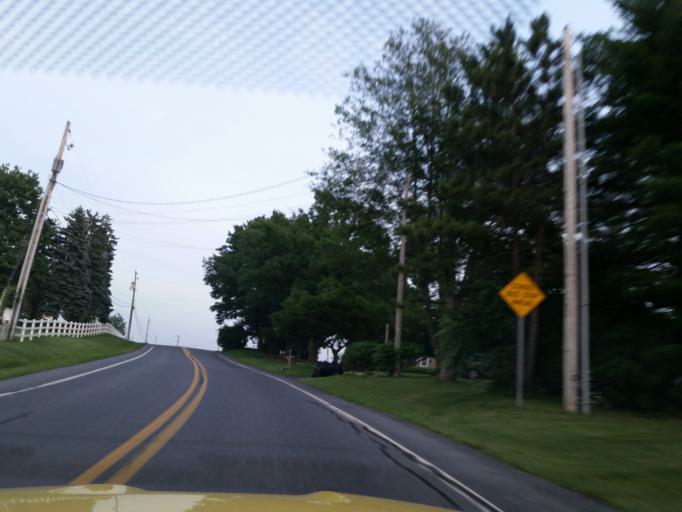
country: US
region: Pennsylvania
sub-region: Lebanon County
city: Palmyra
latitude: 40.4127
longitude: -76.6056
